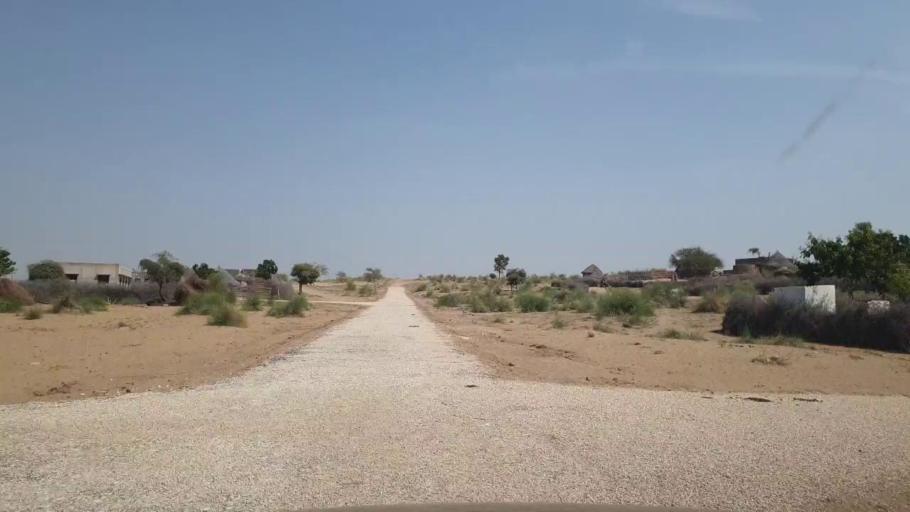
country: PK
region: Sindh
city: Islamkot
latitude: 25.1026
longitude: 70.7649
